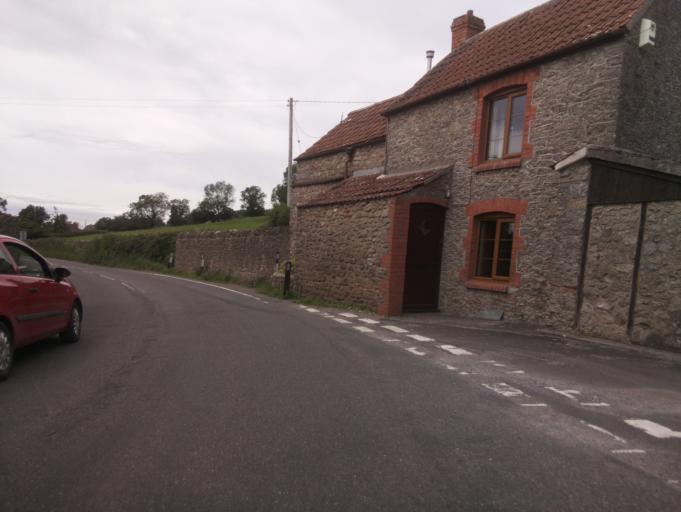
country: GB
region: England
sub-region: Somerset
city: Wells
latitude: 51.2329
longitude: -2.7082
